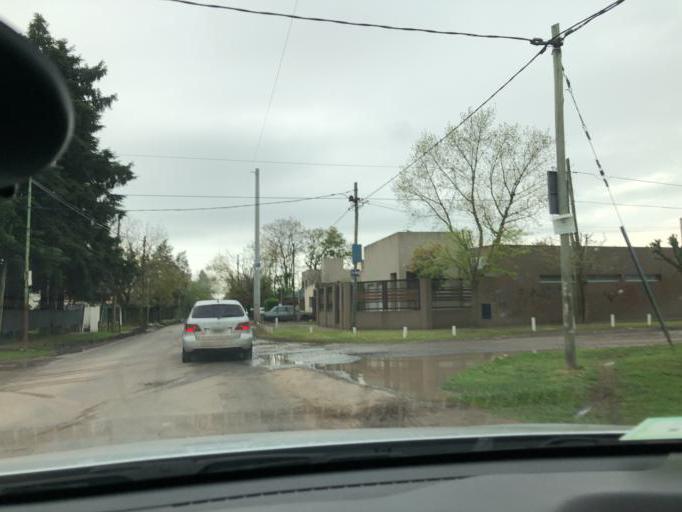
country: AR
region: Buenos Aires
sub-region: Partido de La Plata
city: La Plata
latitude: -34.8955
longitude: -58.0663
